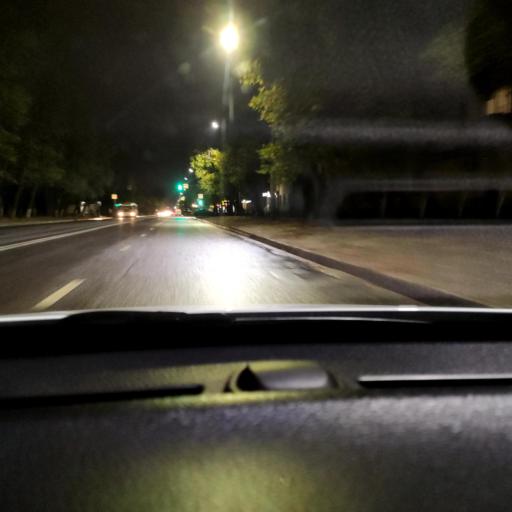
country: RU
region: Voronezj
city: Somovo
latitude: 51.7172
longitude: 39.2741
